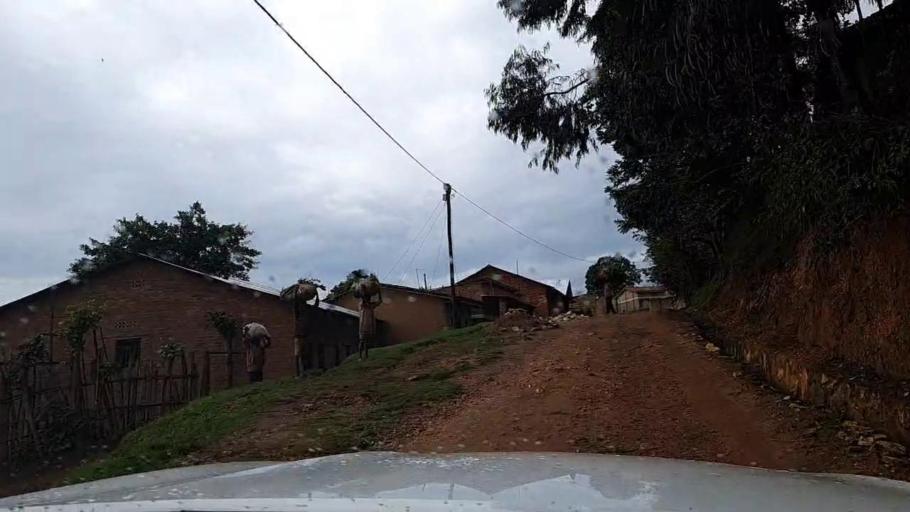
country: RW
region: Southern Province
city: Nzega
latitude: -2.4575
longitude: 29.4672
